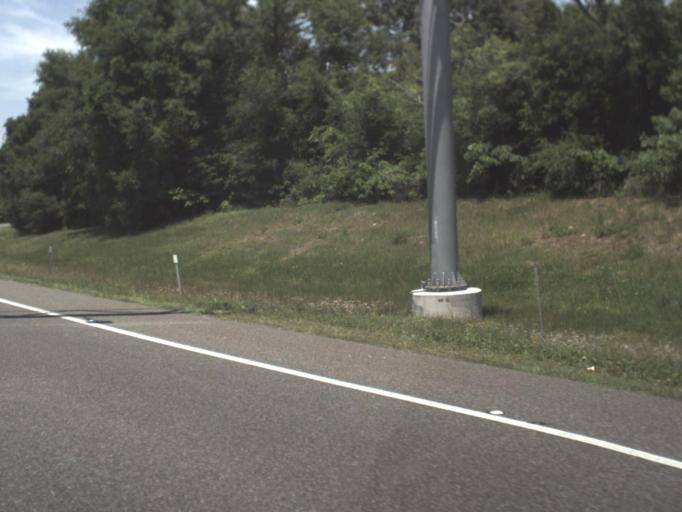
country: US
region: Florida
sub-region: Duval County
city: Jacksonville
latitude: 30.4461
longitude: -81.6086
